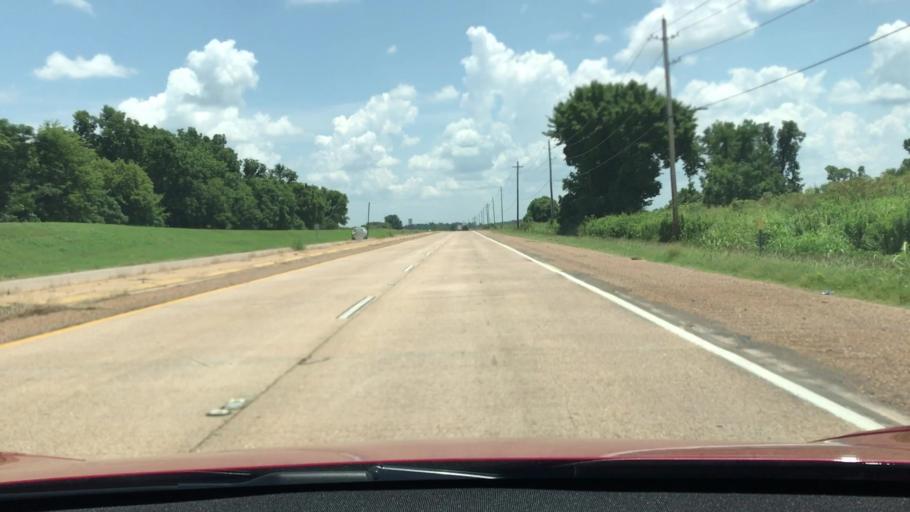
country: US
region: Louisiana
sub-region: Bossier Parish
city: Bossier City
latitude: 32.3968
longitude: -93.6897
